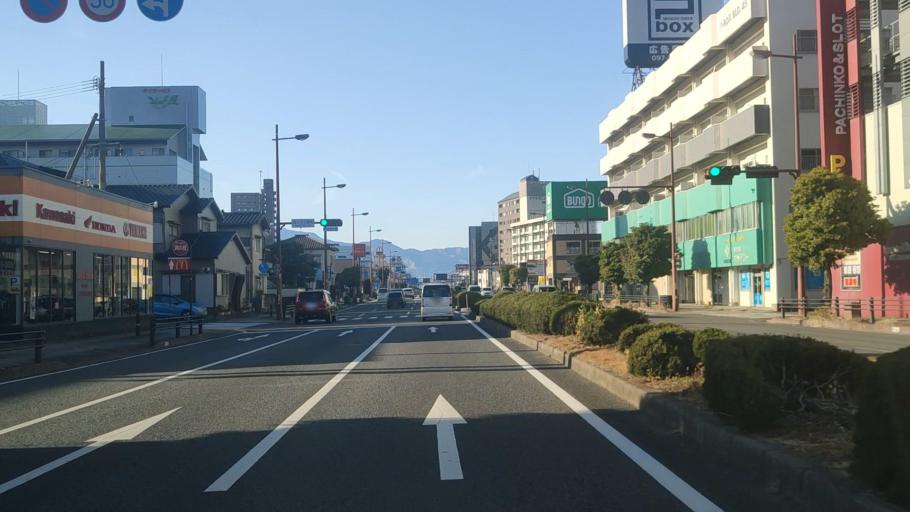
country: JP
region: Oita
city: Oita
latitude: 33.2440
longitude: 131.5874
